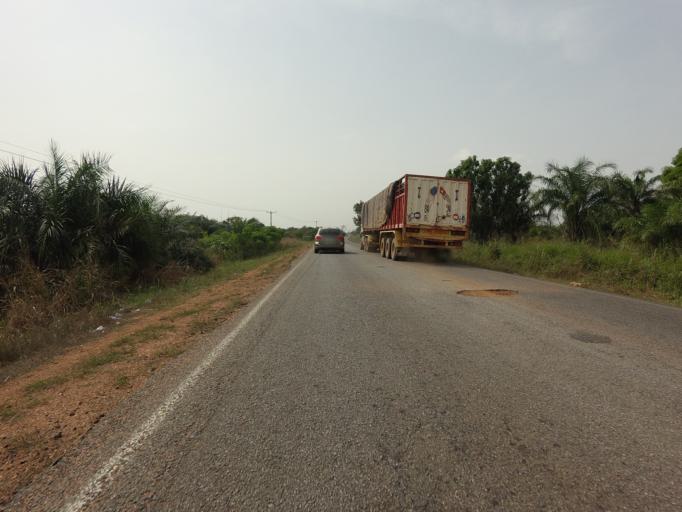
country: GH
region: Volta
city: Ho
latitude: 6.3556
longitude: 0.1770
